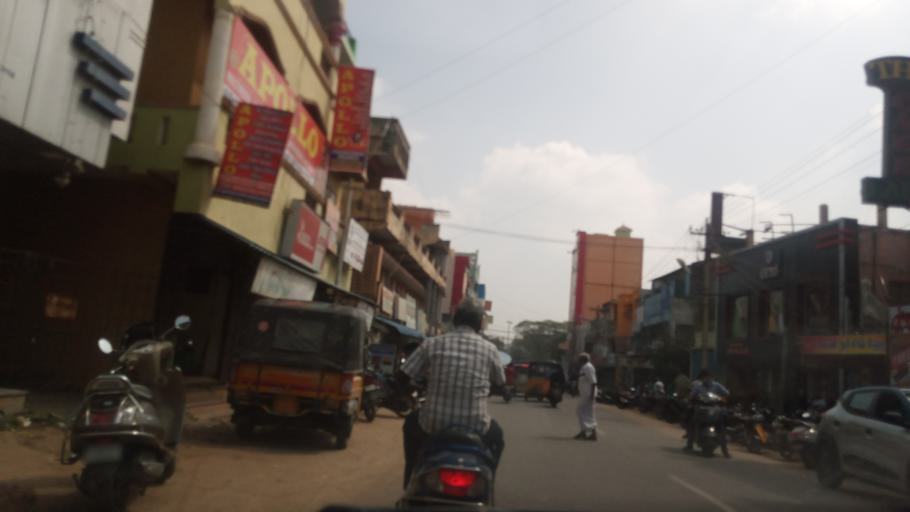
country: IN
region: Tamil Nadu
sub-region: Vellore
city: Arakkonam
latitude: 13.0858
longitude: 79.6636
